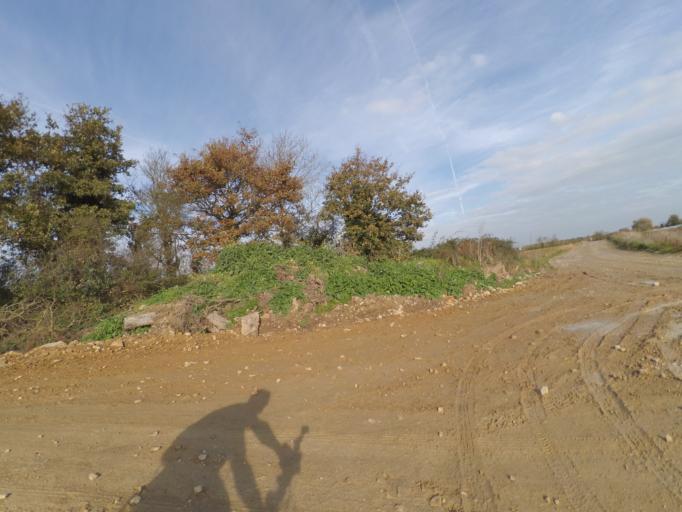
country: FR
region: Pays de la Loire
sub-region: Departement de la Vendee
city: Saint-Hilaire-de-Loulay
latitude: 47.0056
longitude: -1.3613
